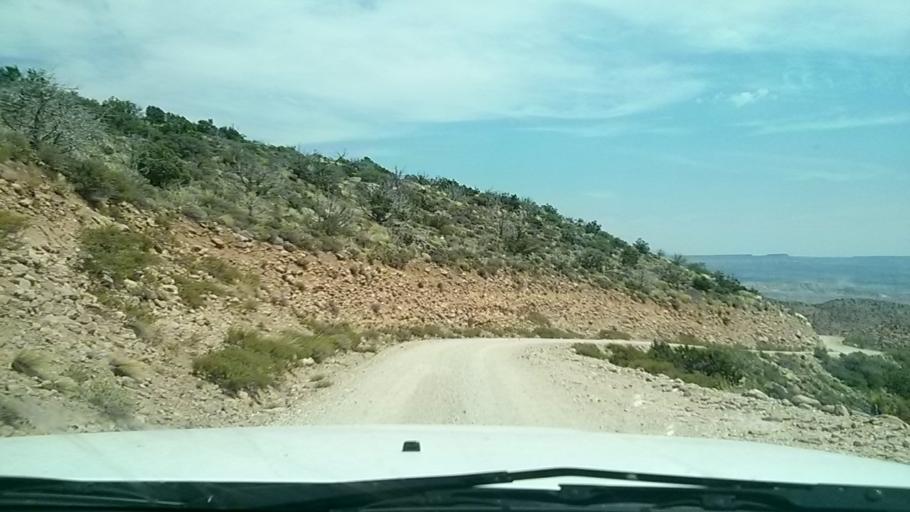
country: US
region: Utah
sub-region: Washington County
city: Toquerville
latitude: 37.2728
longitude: -113.3961
